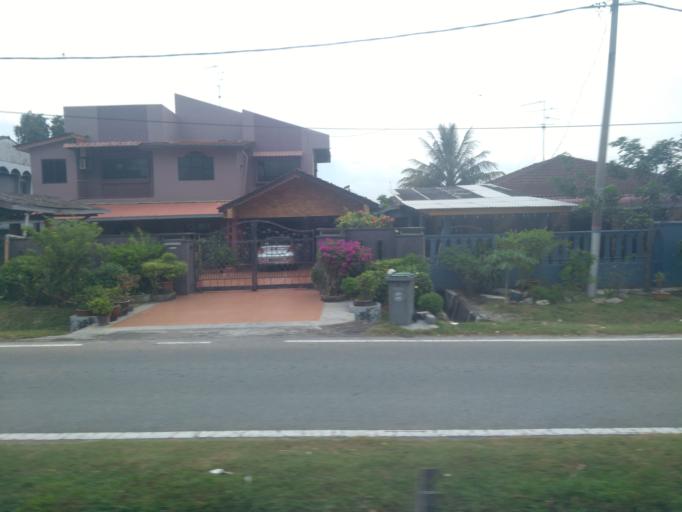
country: MY
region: Johor
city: Skudai
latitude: 1.4996
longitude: 103.6971
